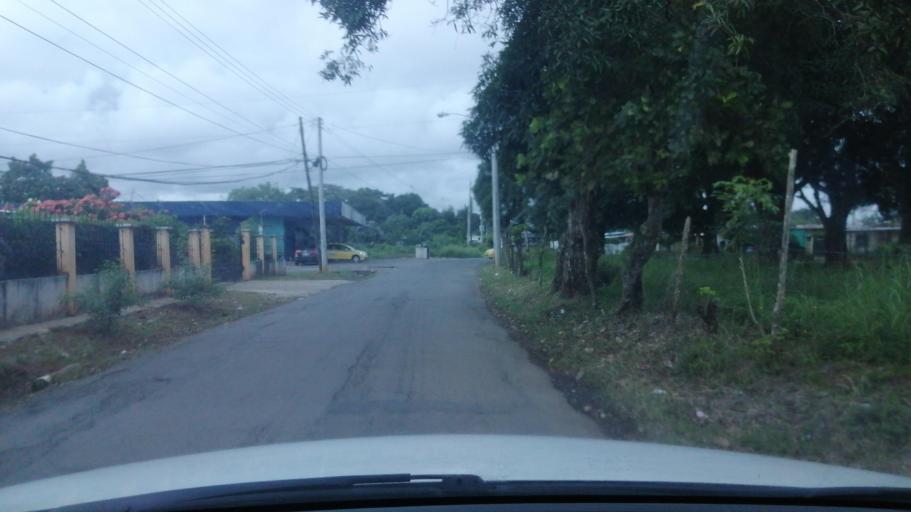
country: PA
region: Chiriqui
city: David
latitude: 8.4013
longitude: -82.4409
